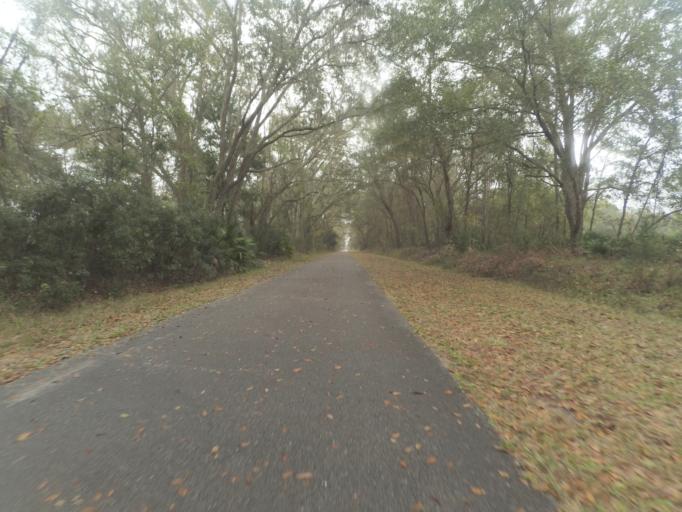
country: US
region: Florida
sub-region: Alachua County
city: Hawthorne
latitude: 29.5921
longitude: -82.1912
